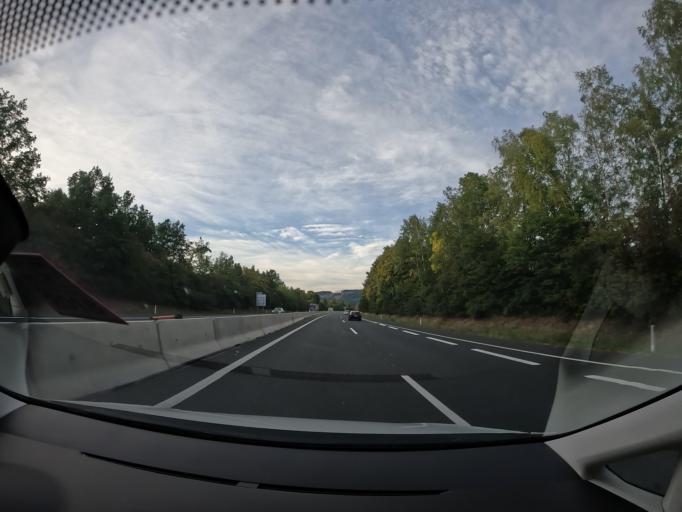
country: AT
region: Carinthia
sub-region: Politischer Bezirk Wolfsberg
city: Wolfsberg
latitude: 46.8306
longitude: 14.8183
